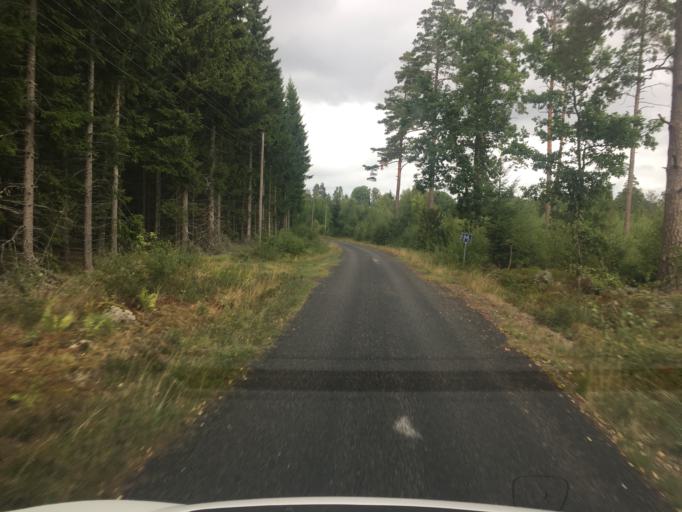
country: SE
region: Kronoberg
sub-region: Ljungby Kommun
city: Lagan
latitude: 56.9463
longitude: 14.0335
